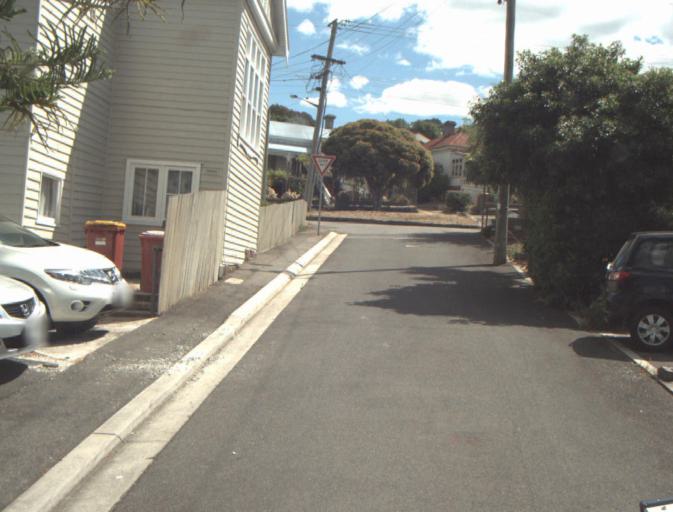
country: AU
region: Tasmania
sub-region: Launceston
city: West Launceston
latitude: -41.4477
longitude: 147.1332
